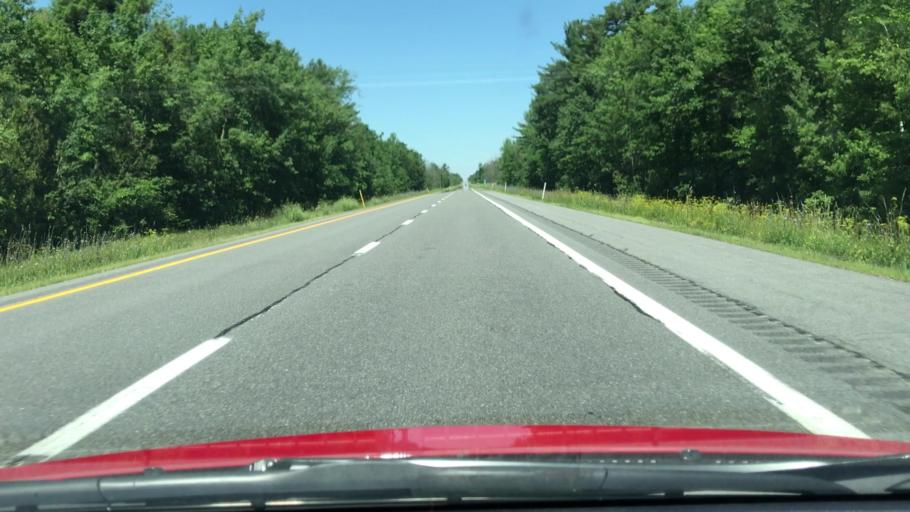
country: US
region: New York
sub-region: Clinton County
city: Champlain
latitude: 44.9348
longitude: -73.4466
